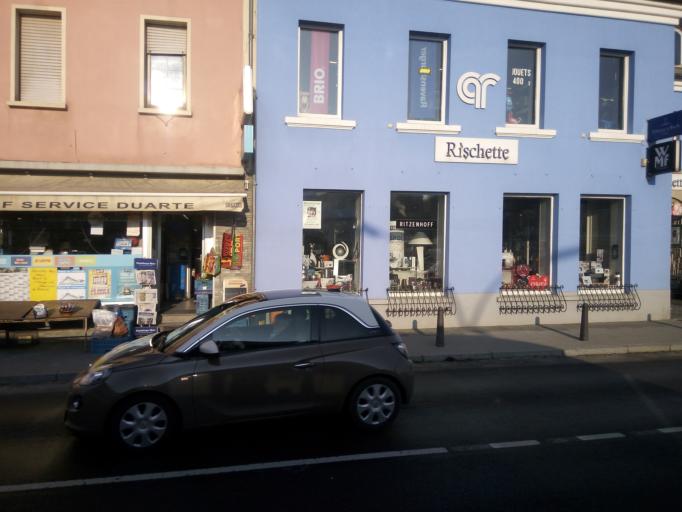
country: LU
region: Grevenmacher
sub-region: Canton de Grevenmacher
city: Junglinster
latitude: 49.7119
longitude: 6.2518
